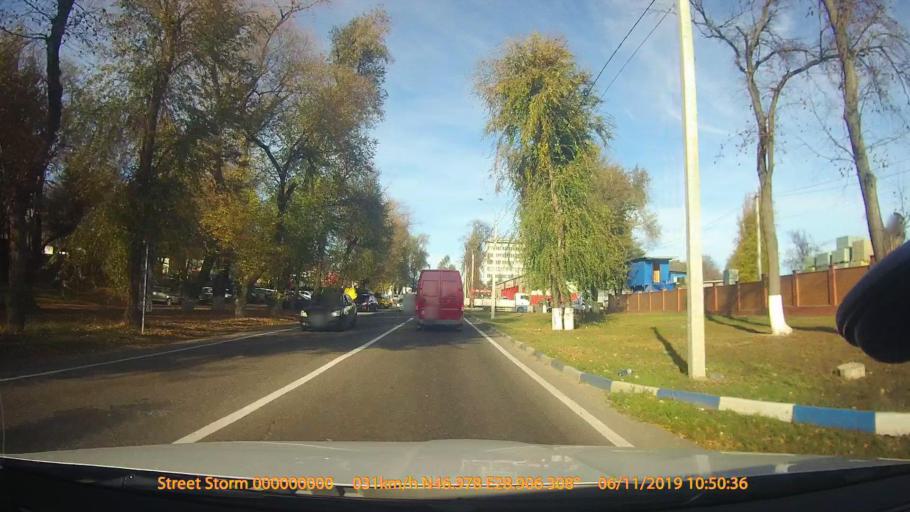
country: MD
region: Chisinau
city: Chisinau
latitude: 46.9778
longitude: 28.9061
